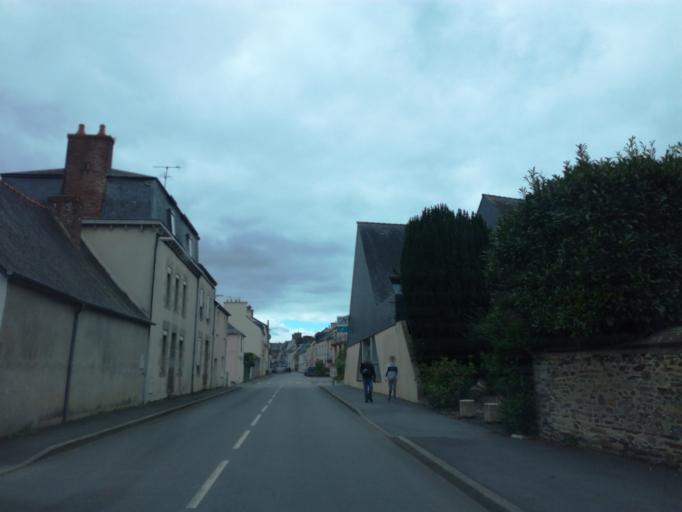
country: FR
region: Brittany
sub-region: Departement des Cotes-d'Armor
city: Loudeac
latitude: 48.1770
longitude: -2.7490
